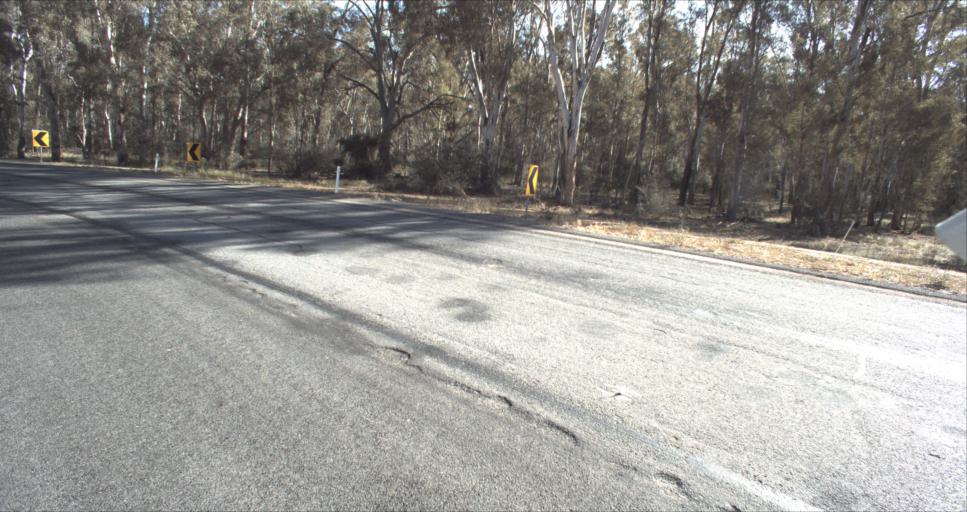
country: AU
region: New South Wales
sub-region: Leeton
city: Leeton
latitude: -34.6320
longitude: 146.3746
